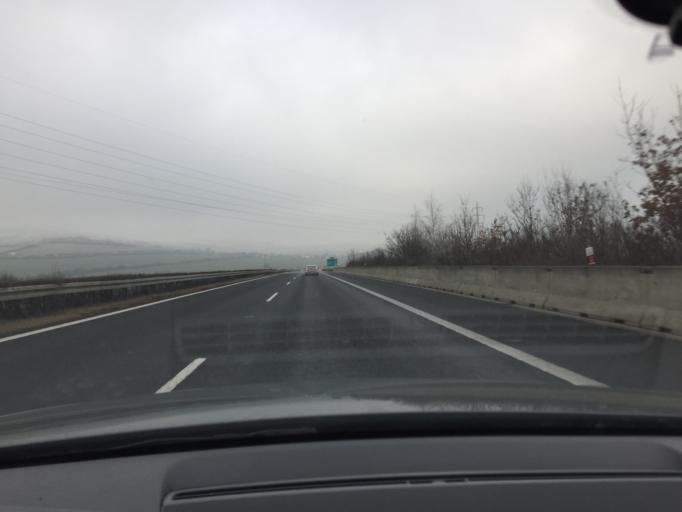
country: CZ
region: Ustecky
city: Lovosice
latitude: 50.5063
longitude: 14.0429
